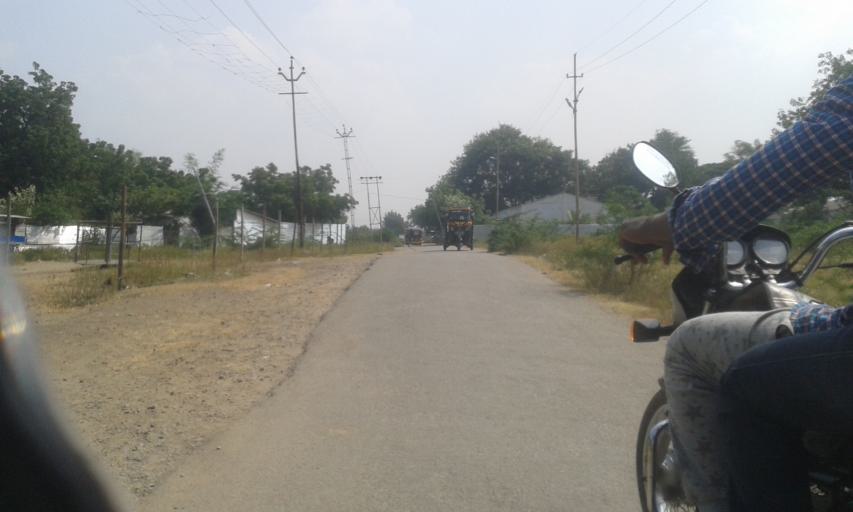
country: IN
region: Karnataka
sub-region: Raichur
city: Lingsugur
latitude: 16.1938
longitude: 76.6602
